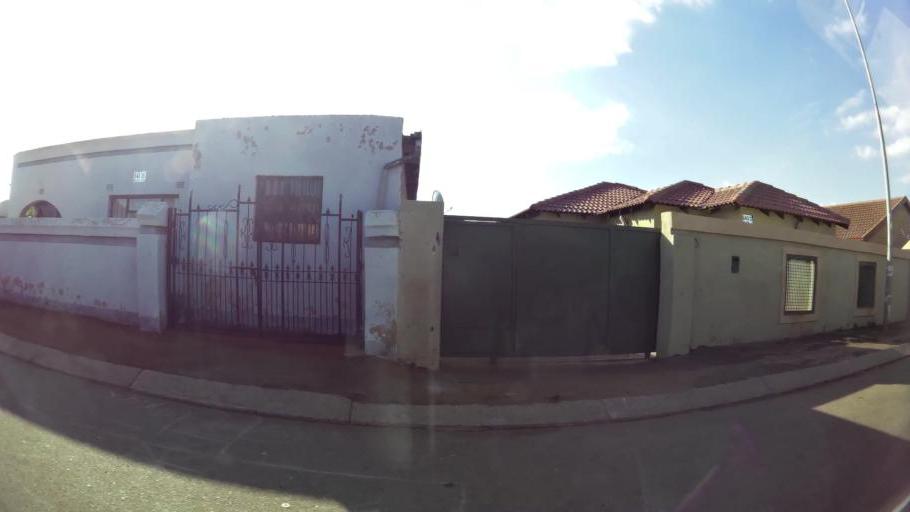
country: ZA
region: Gauteng
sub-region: City of Johannesburg Metropolitan Municipality
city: Soweto
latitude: -26.2537
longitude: 27.9127
